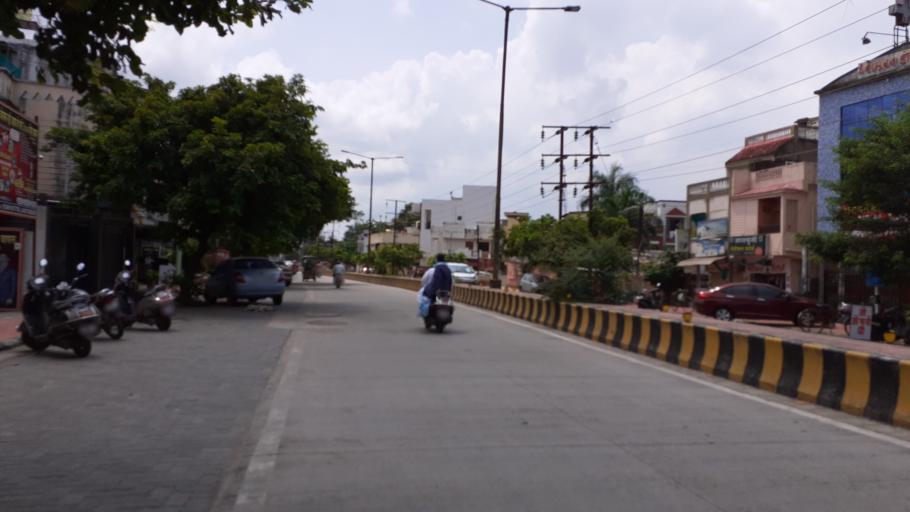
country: IN
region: Maharashtra
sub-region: Nagpur Division
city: Nagpur
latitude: 21.1264
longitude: 79.1189
